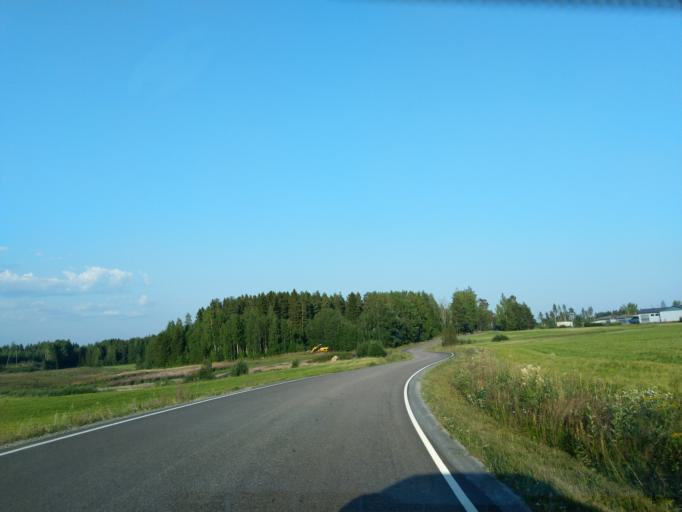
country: FI
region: Satakunta
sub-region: Pohjois-Satakunta
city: Kankaanpaeae
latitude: 61.8164
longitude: 22.3433
